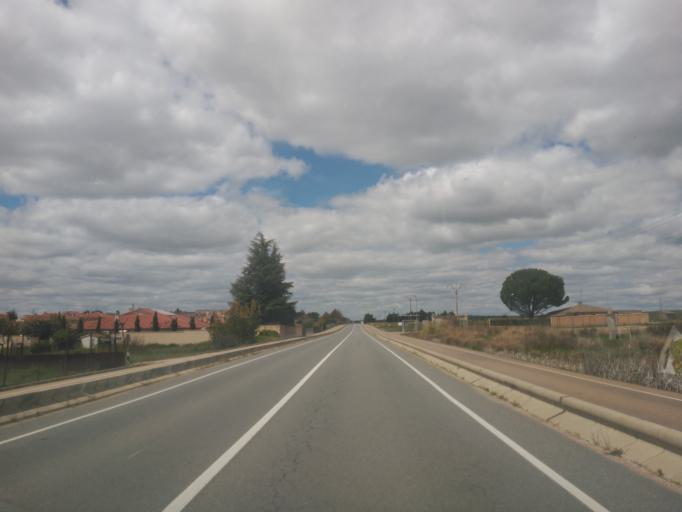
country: ES
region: Castille and Leon
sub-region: Provincia de Salamanca
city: Villamayor
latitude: 41.0117
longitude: -5.7097
